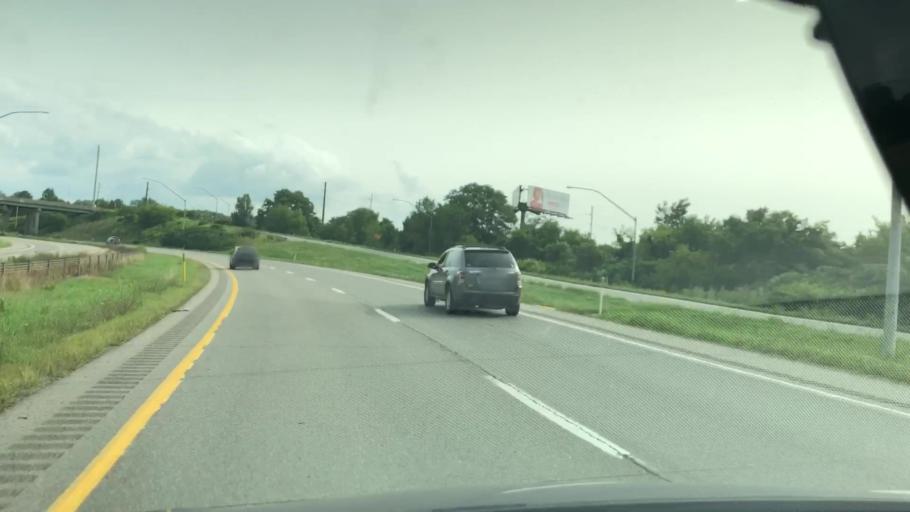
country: US
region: Pennsylvania
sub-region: Erie County
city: Erie
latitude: 42.0970
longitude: -80.1226
